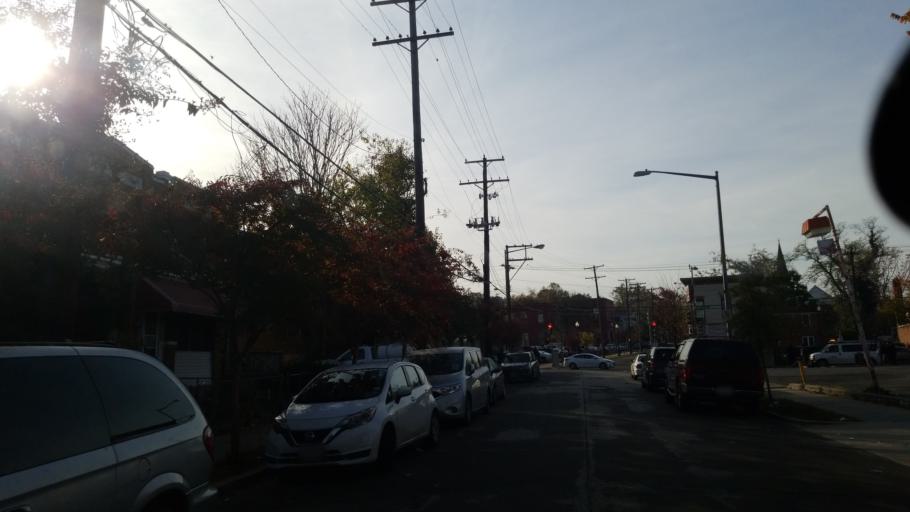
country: US
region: Maryland
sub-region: Prince George's County
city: Hillcrest Heights
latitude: 38.8674
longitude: -76.9852
